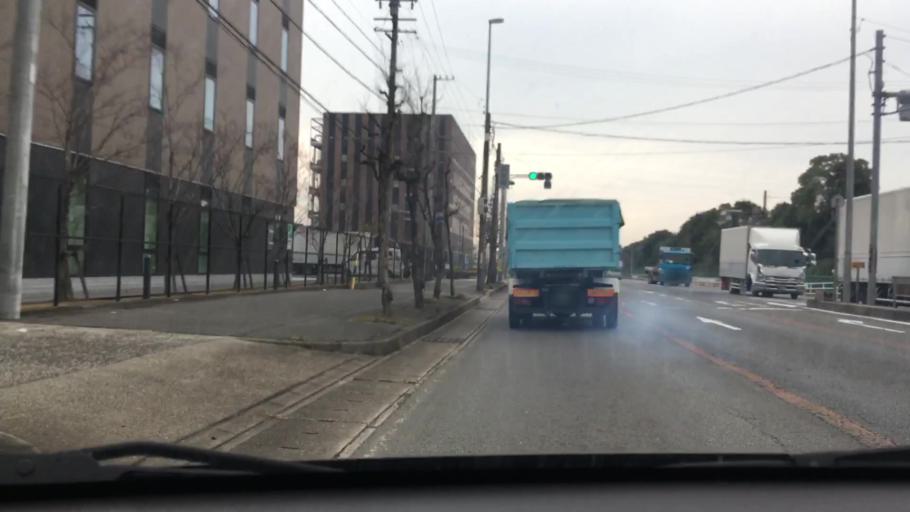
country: JP
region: Mie
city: Yokkaichi
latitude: 34.9306
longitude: 136.6072
